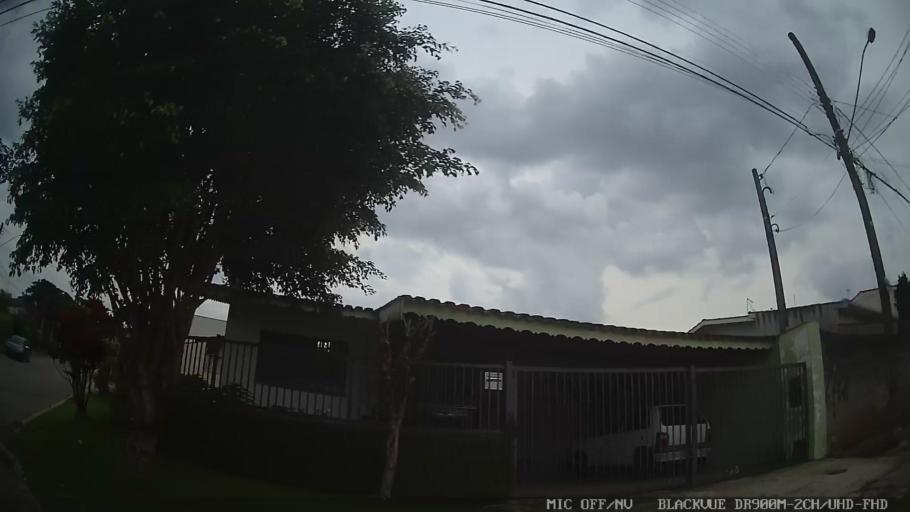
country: BR
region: Sao Paulo
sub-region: Atibaia
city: Atibaia
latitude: -23.1343
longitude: -46.5607
